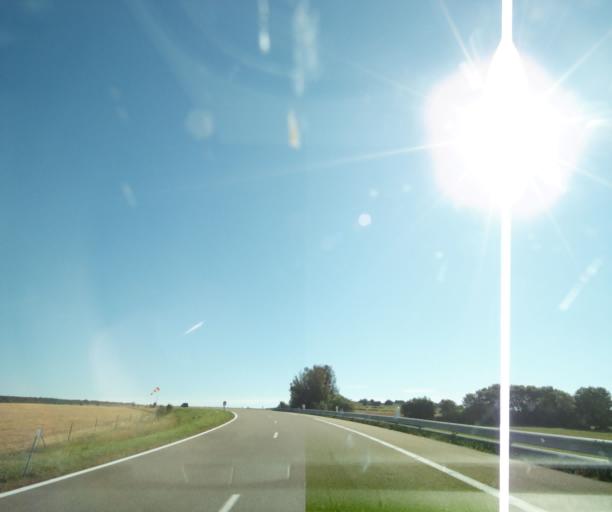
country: FR
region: Champagne-Ardenne
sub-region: Departement de la Haute-Marne
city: Rolampont
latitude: 47.9096
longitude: 5.2266
